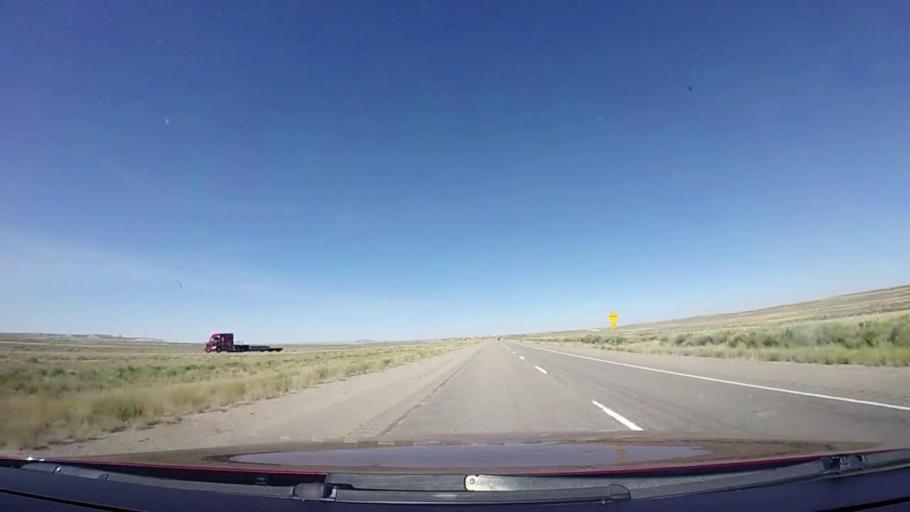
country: US
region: Wyoming
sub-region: Sweetwater County
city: Rock Springs
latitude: 41.6333
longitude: -108.3729
